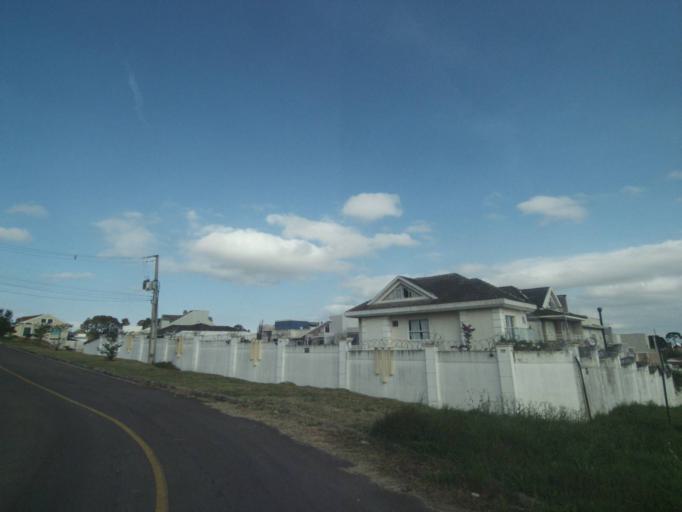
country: BR
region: Parana
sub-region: Pinhais
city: Pinhais
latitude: -25.4106
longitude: -49.2136
